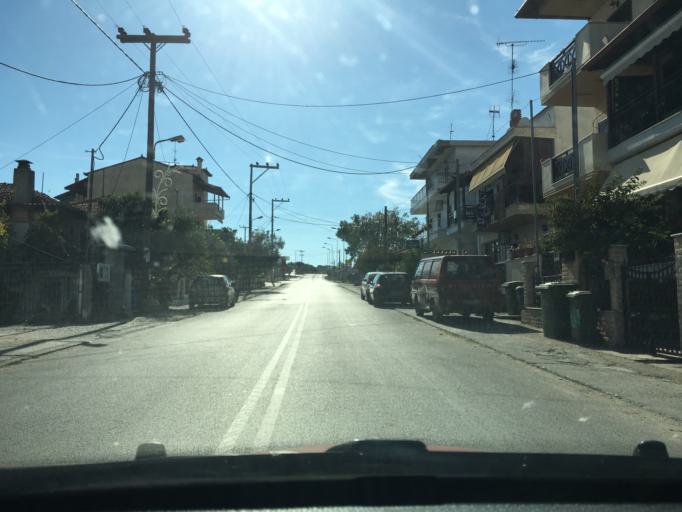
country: GR
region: Central Macedonia
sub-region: Nomos Chalkidikis
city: Ierissos
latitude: 40.3957
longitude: 23.8745
